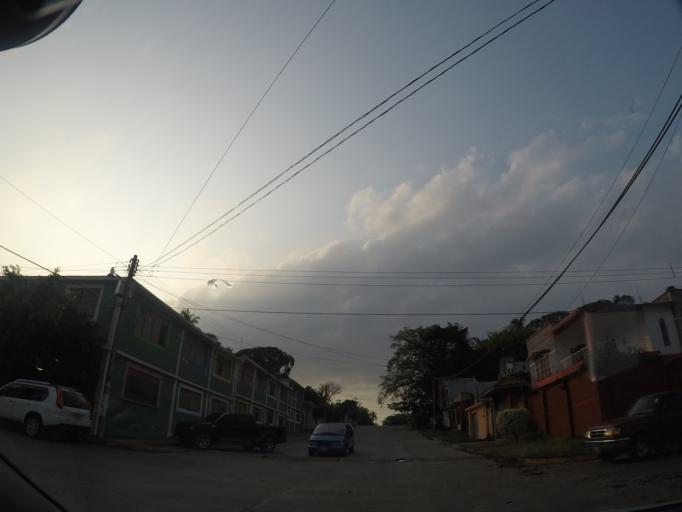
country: MX
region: Oaxaca
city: Matias Romero
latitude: 16.8733
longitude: -95.0439
